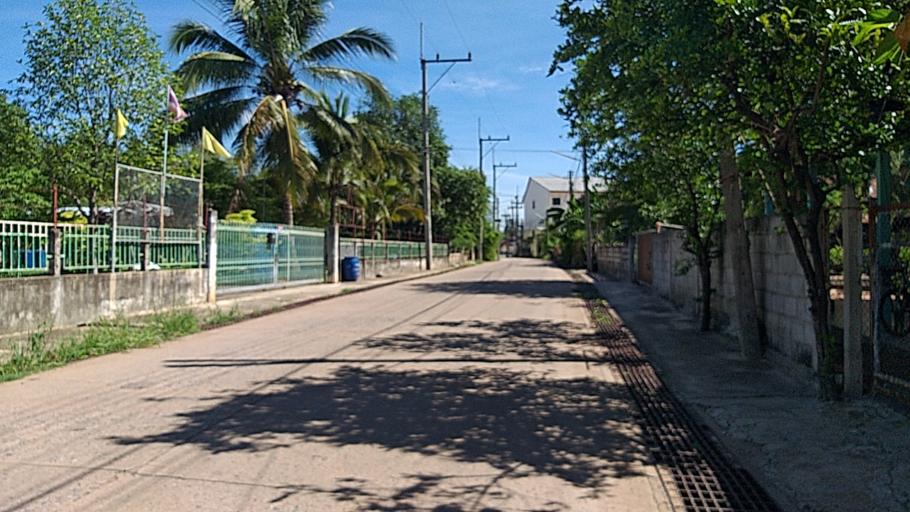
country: TH
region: Chaiyaphum
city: Ban Thaen
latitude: 16.4080
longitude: 102.3532
